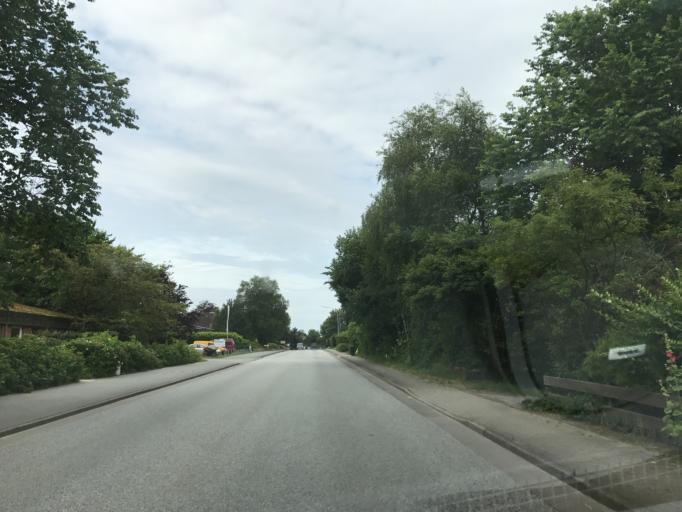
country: DE
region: Schleswig-Holstein
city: Nindorf
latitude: 54.0875
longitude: 9.1068
